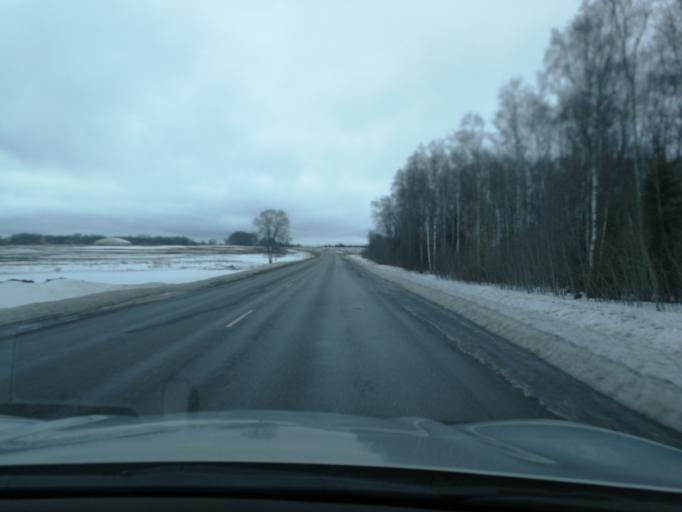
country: EE
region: Harju
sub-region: Anija vald
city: Kehra
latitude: 59.3910
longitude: 25.2873
